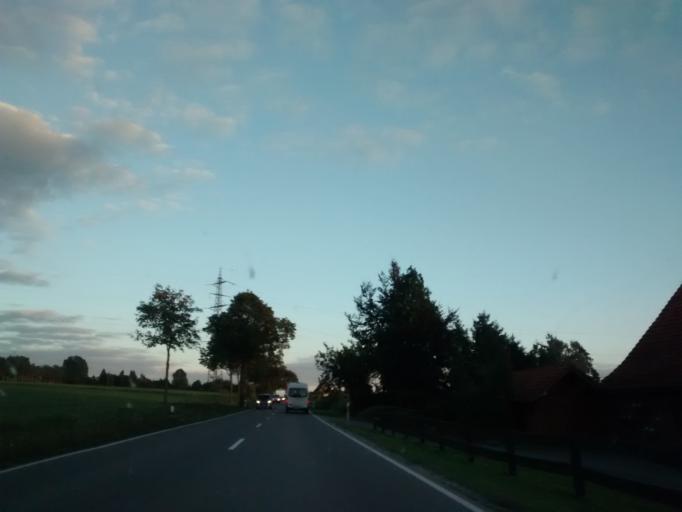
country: DE
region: North Rhine-Westphalia
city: Halle
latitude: 52.0736
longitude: 8.3316
